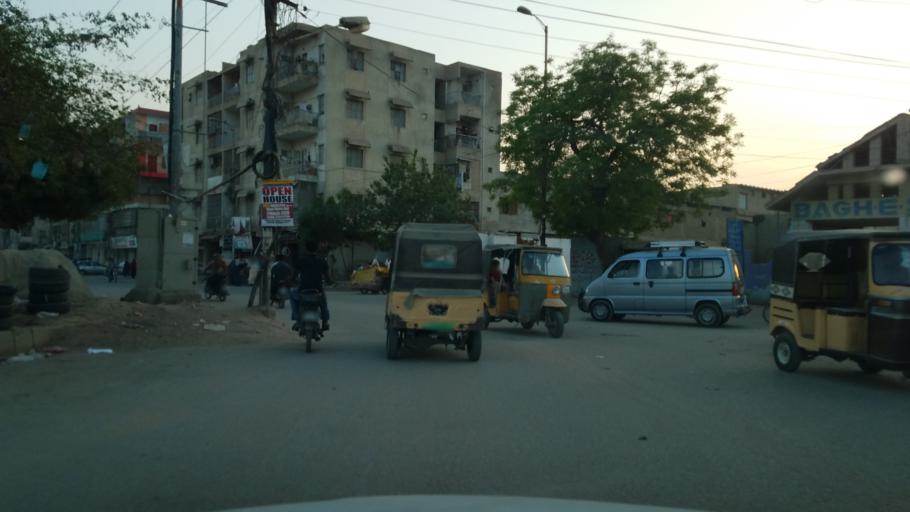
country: PK
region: Sindh
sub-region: Karachi District
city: Karachi
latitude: 24.9465
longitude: 67.0773
